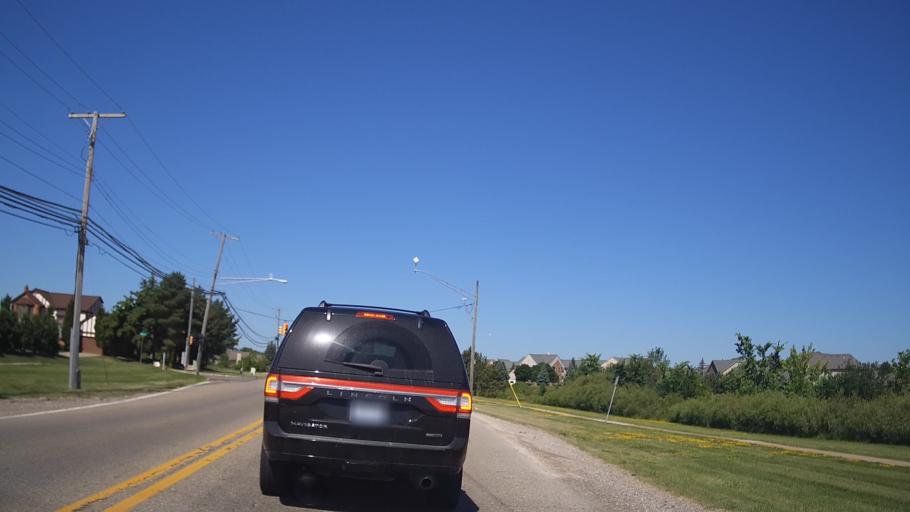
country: US
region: Michigan
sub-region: Macomb County
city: Sterling Heights
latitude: 42.5934
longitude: -83.0797
